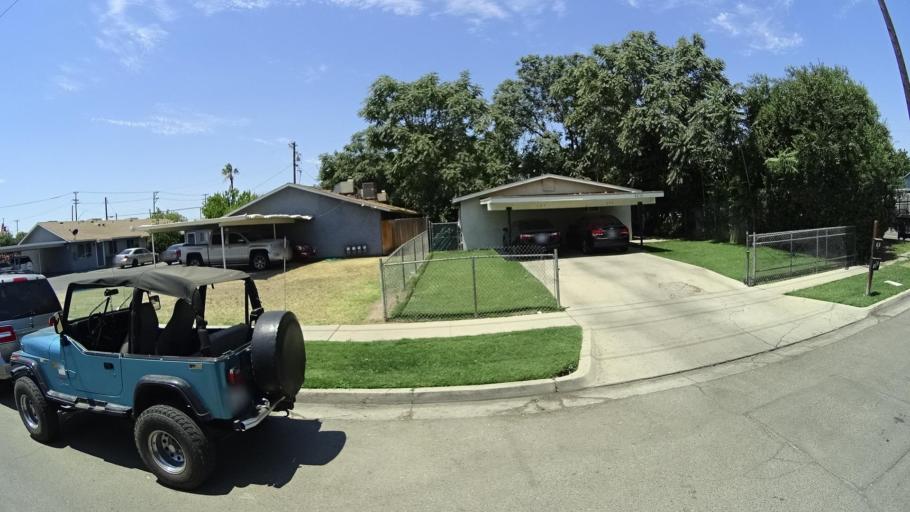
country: US
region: California
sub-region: Fresno County
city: Fresno
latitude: 36.7221
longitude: -119.7659
